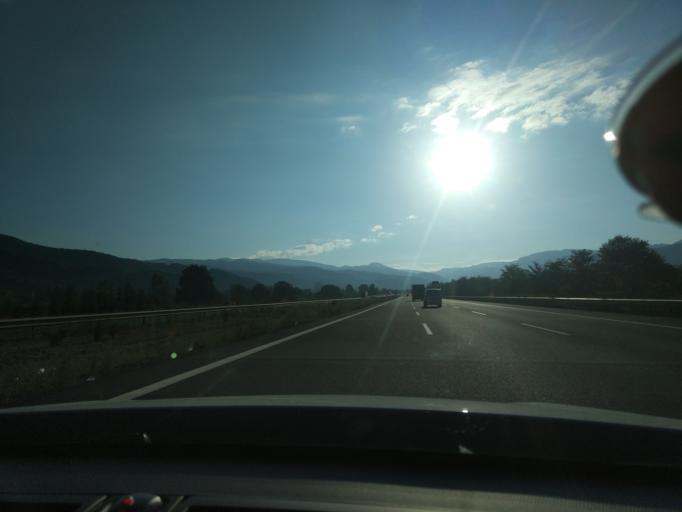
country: TR
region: Duzce
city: Kaynasli
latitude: 40.7832
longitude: 31.3085
